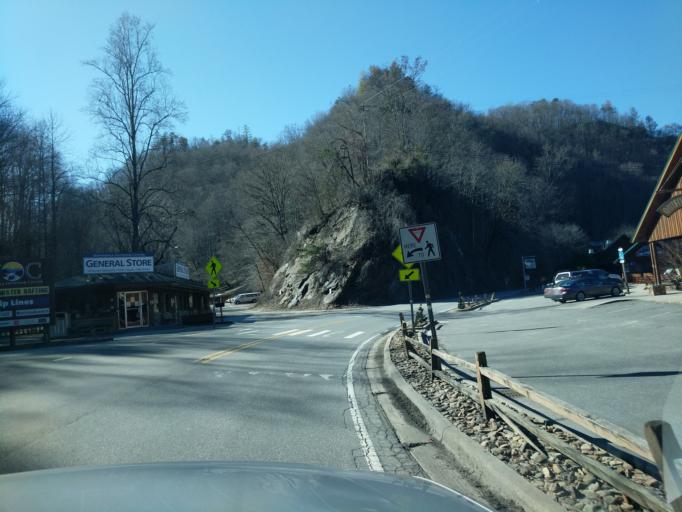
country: US
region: North Carolina
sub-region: Swain County
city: Bryson City
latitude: 35.3314
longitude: -83.5910
